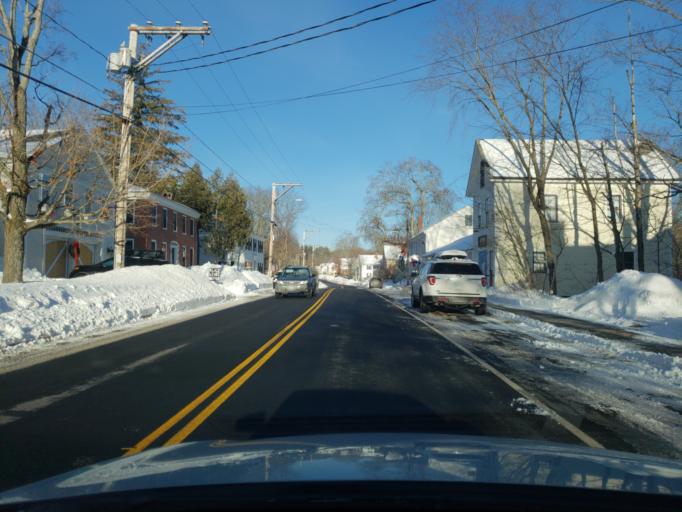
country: US
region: New Hampshire
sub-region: Hillsborough County
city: Greenfield
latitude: 42.9890
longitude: -71.8137
